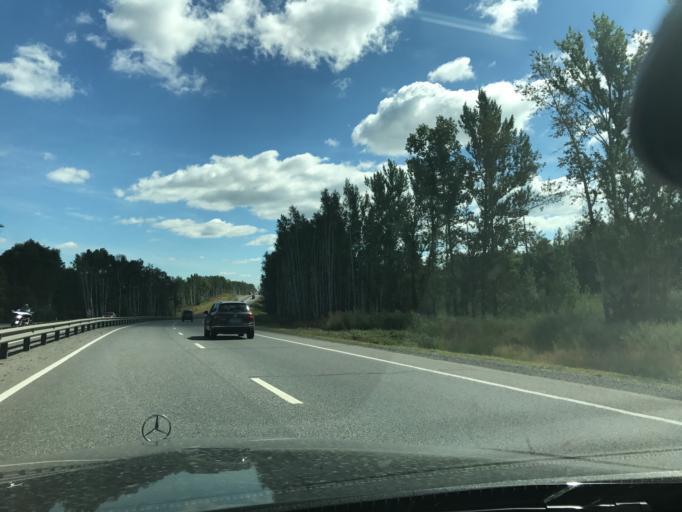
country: RU
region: Vladimir
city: Novovyazniki
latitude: 56.2026
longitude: 42.3513
